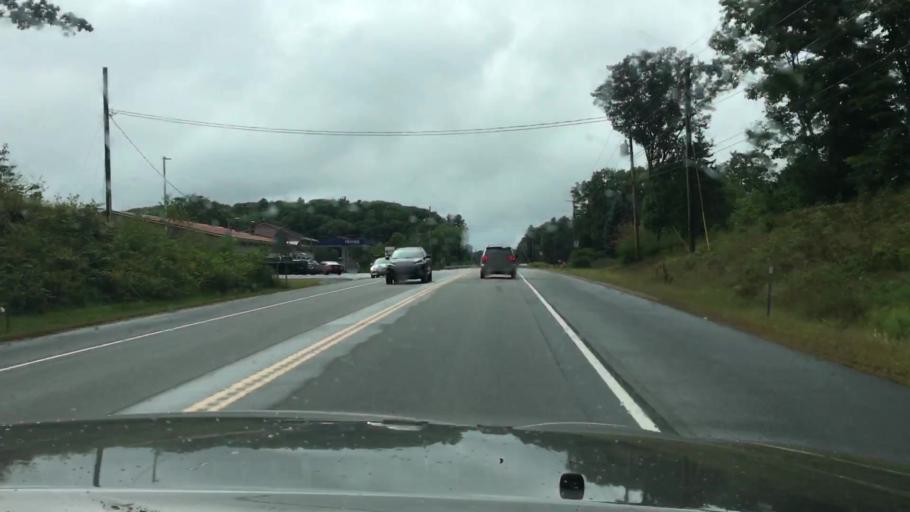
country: US
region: New Hampshire
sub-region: Cheshire County
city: Chesterfield
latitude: 42.9000
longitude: -72.4281
